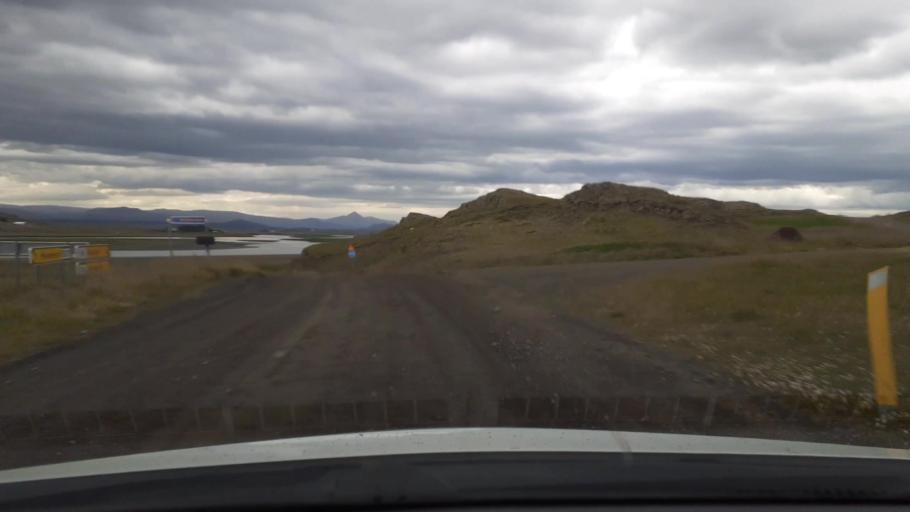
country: IS
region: West
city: Borgarnes
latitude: 64.6009
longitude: -21.6981
